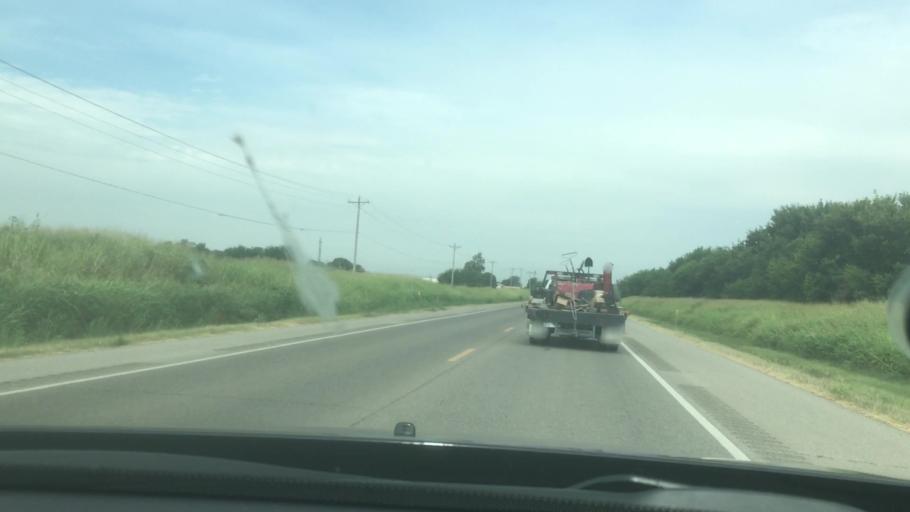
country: US
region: Oklahoma
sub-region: Garvin County
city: Lindsay
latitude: 34.8273
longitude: -97.5583
